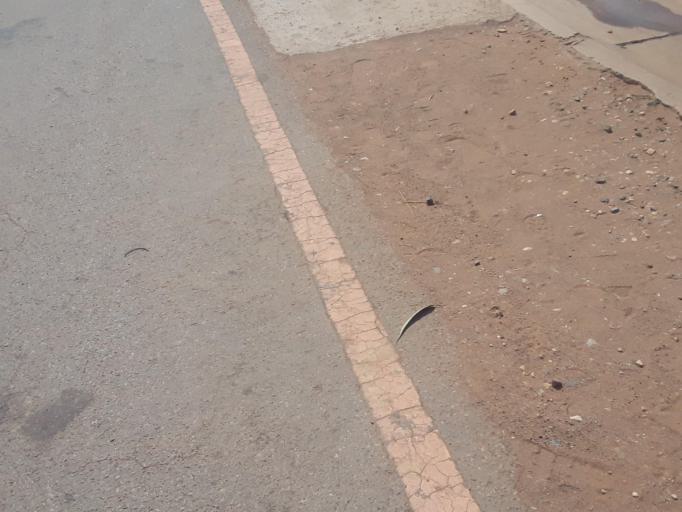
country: ZM
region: Lusaka
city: Lusaka
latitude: -15.3589
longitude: 28.2819
